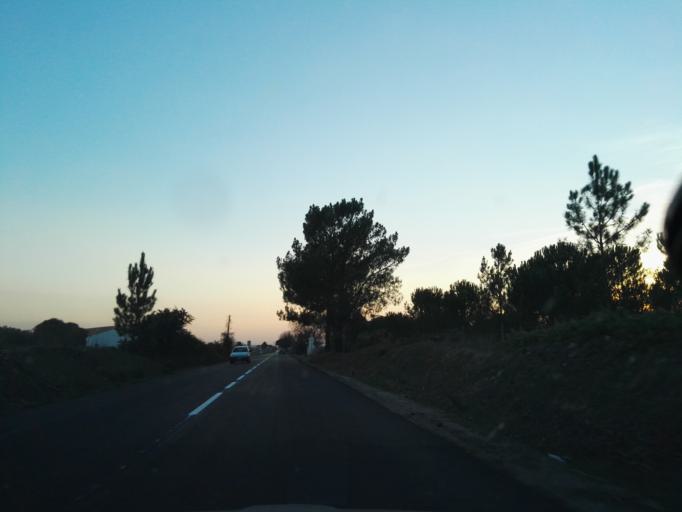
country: PT
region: Santarem
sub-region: Coruche
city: Coruche
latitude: 38.9639
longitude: -8.4848
